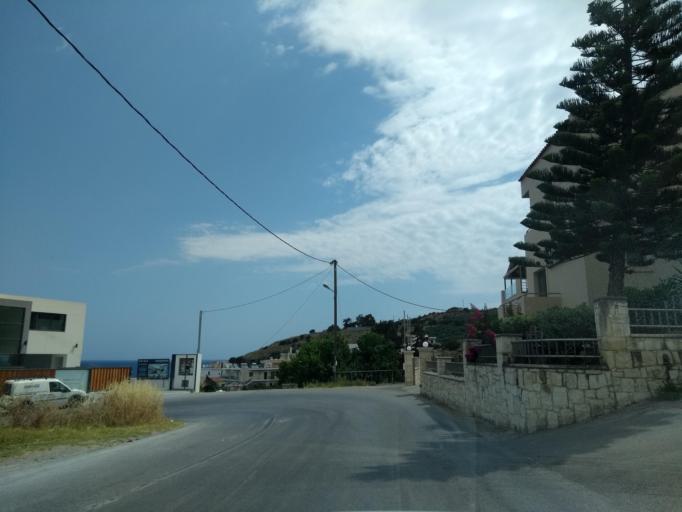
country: GR
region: Crete
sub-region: Nomos Chanias
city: Kalivai
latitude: 35.4489
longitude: 24.1764
